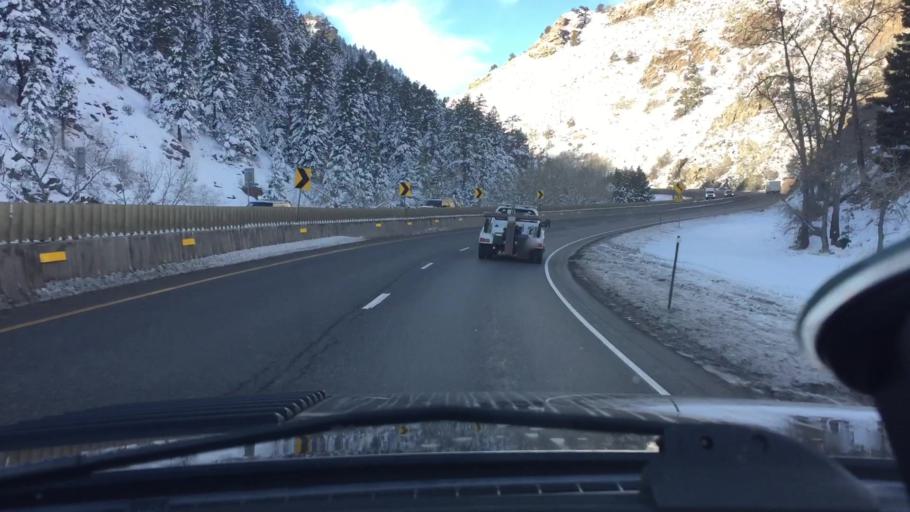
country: US
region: Colorado
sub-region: Jefferson County
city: Indian Hills
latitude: 39.6188
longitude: -105.2098
